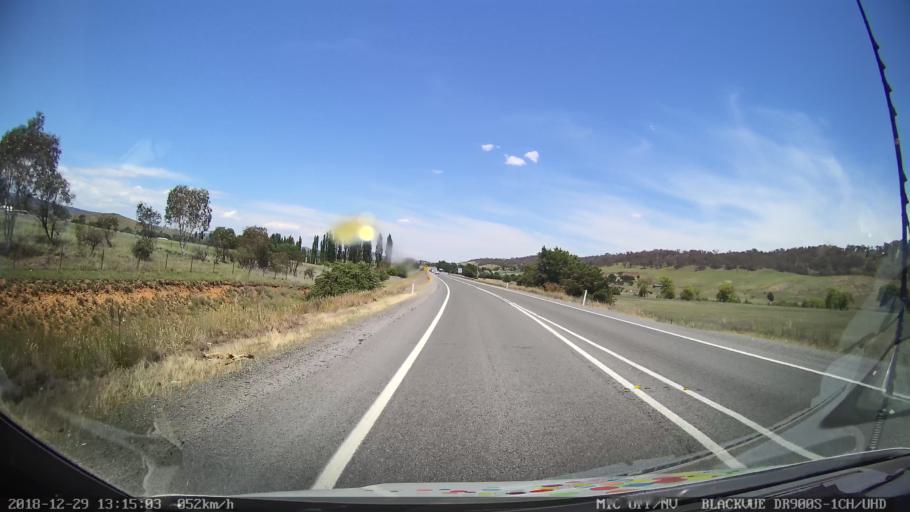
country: AU
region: Australian Capital Territory
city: Macarthur
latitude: -35.7044
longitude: 149.1583
